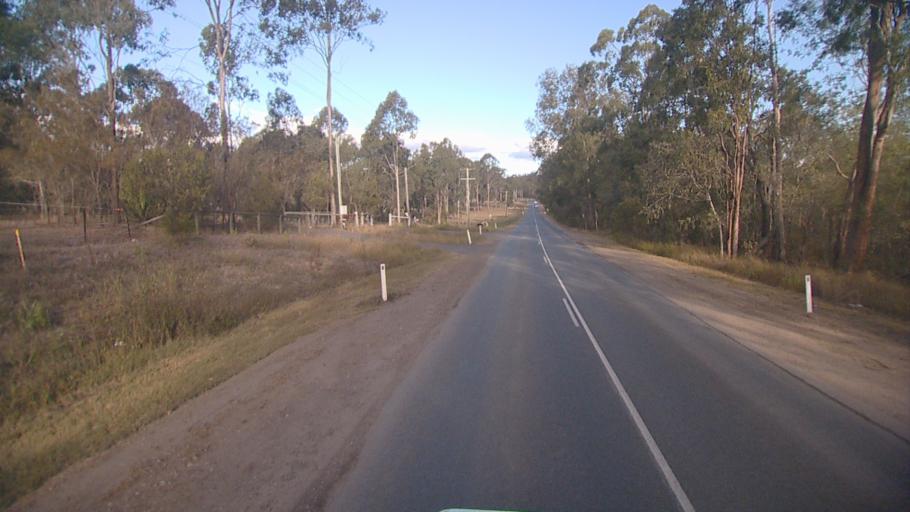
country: AU
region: Queensland
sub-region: Logan
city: Cedar Vale
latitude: -27.8574
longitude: 153.0542
